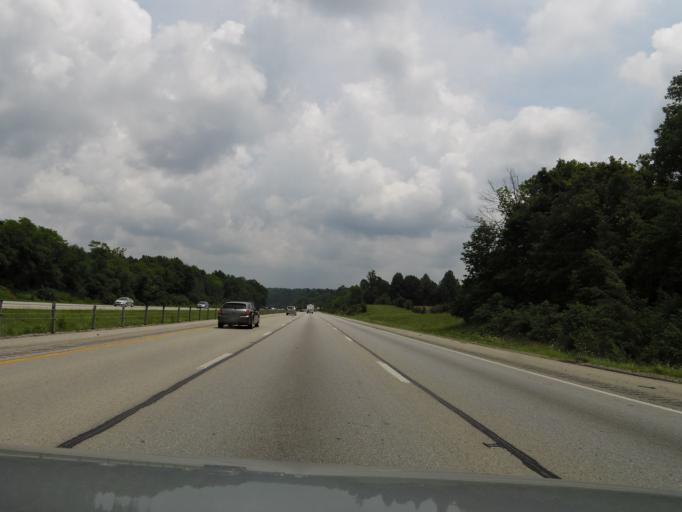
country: US
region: Kentucky
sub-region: Hardin County
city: Elizabethtown
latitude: 37.7348
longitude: -85.8081
